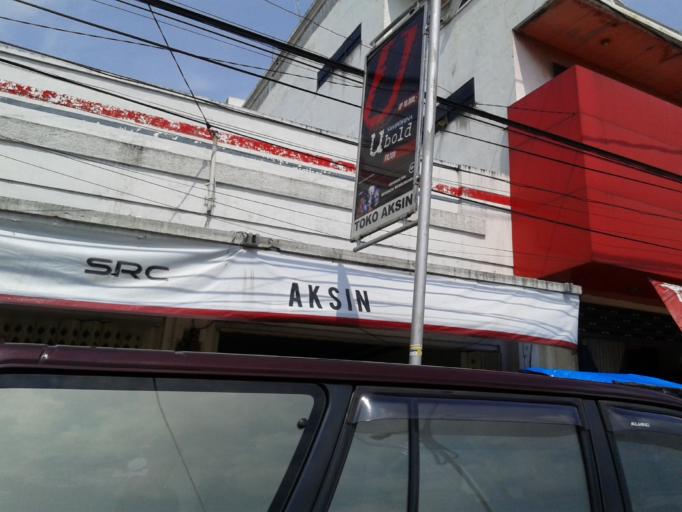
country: ID
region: East Java
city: Lawang
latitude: -7.8298
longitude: 112.7005
